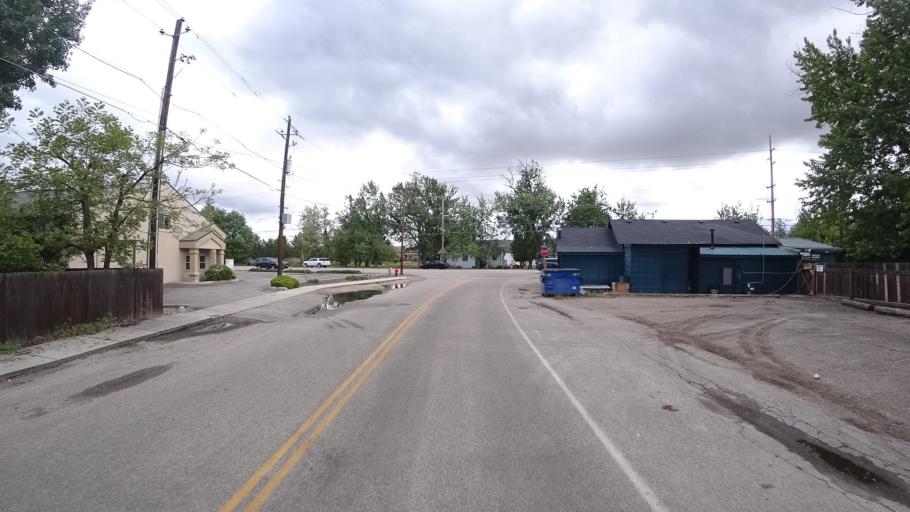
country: US
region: Idaho
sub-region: Ada County
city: Eagle
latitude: 43.6767
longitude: -116.2988
